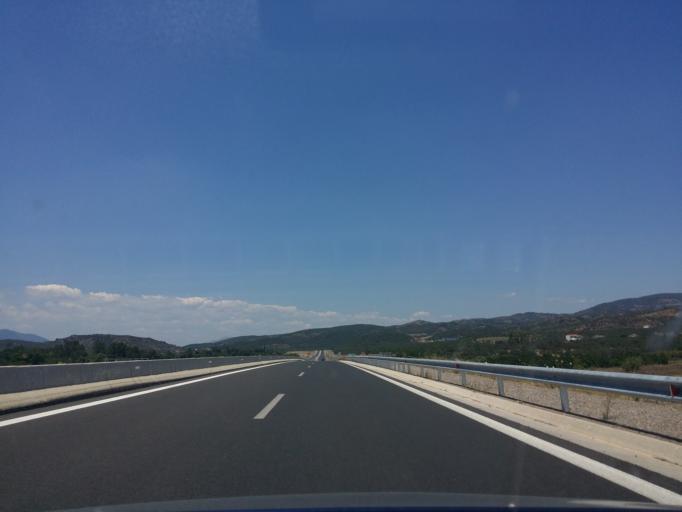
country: GR
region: Peloponnese
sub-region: Nomos Lakonias
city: Sparti
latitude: 37.1002
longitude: 22.4264
